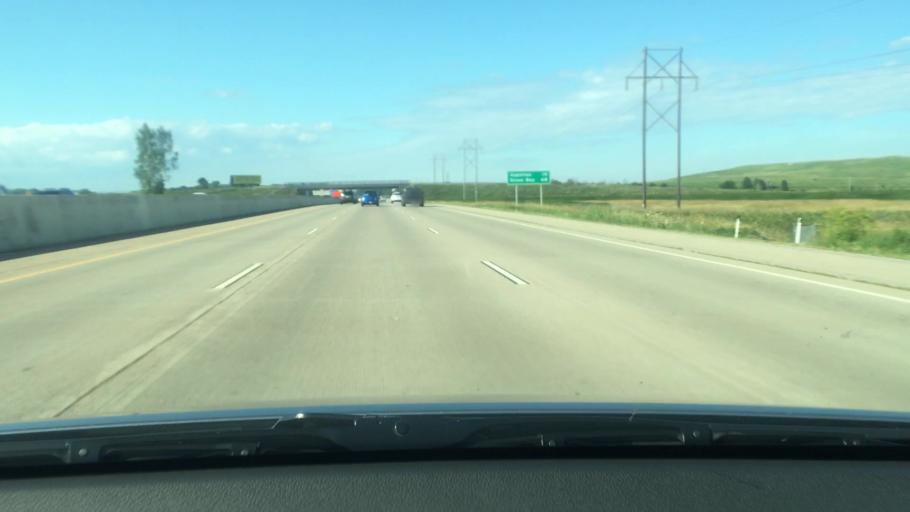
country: US
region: Wisconsin
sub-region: Winnebago County
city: Oshkosh
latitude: 44.0793
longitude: -88.5625
